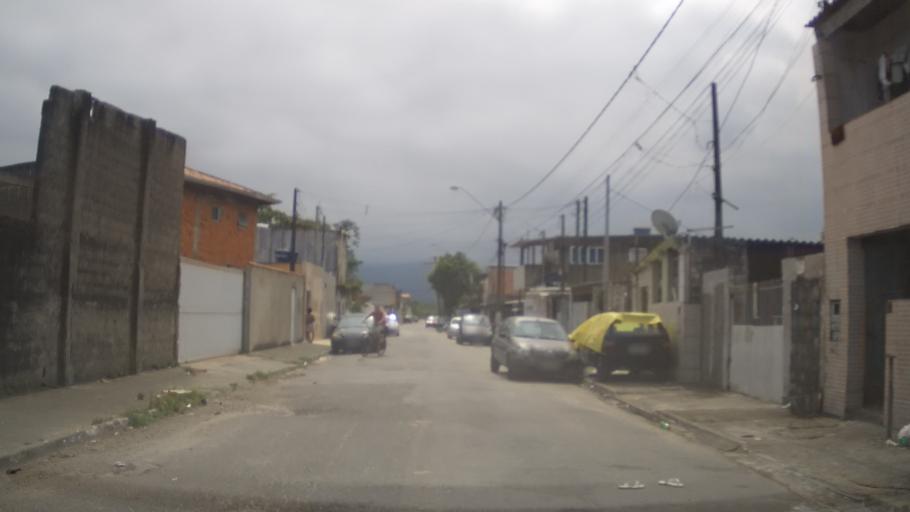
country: BR
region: Sao Paulo
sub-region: Praia Grande
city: Praia Grande
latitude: -23.9971
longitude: -46.4472
